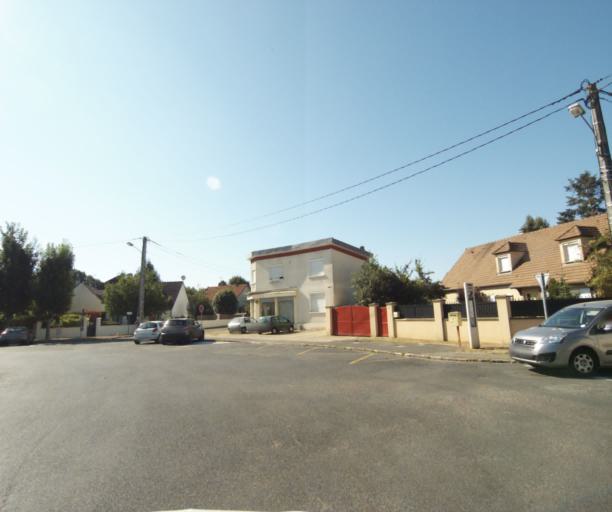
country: FR
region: Ile-de-France
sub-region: Departement de l'Essonne
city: Saint-Vrain
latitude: 48.5332
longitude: 2.3453
